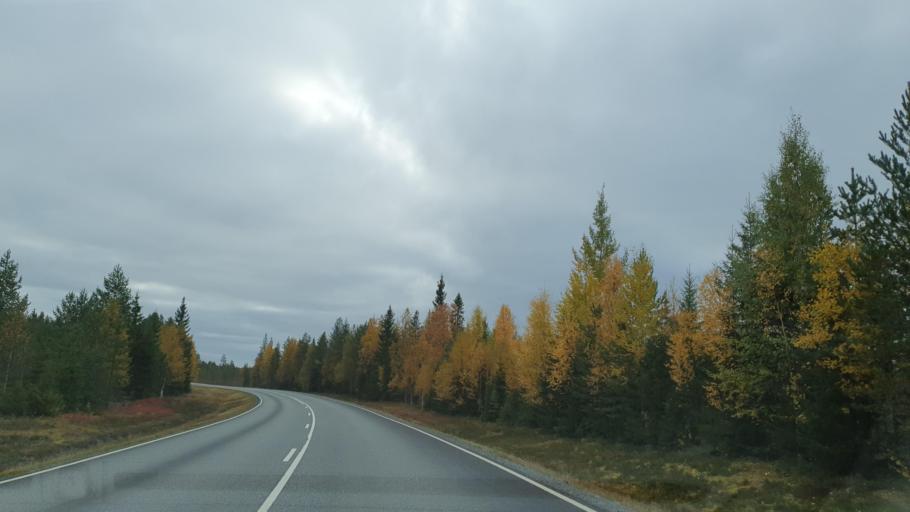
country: FI
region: Lapland
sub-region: Rovaniemi
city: Ranua
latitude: 65.8101
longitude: 26.5555
